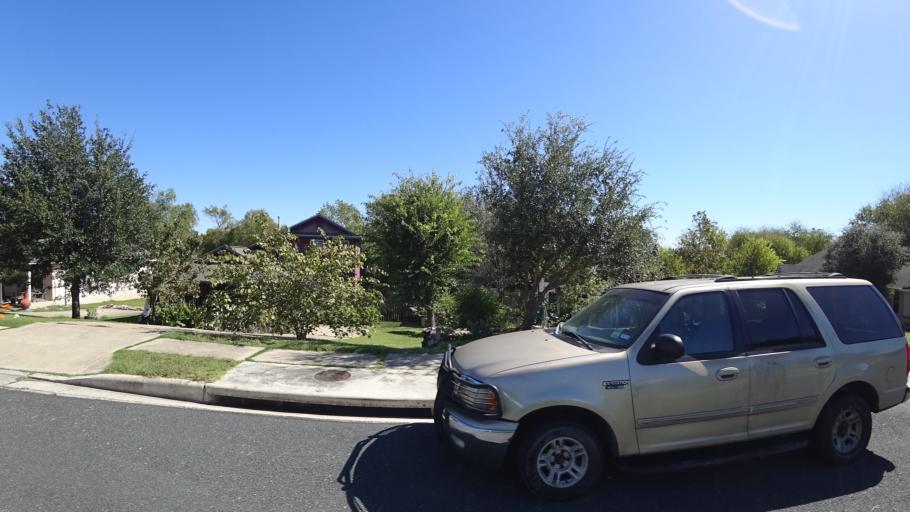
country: US
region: Texas
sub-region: Travis County
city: Hornsby Bend
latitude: 30.2878
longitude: -97.6584
